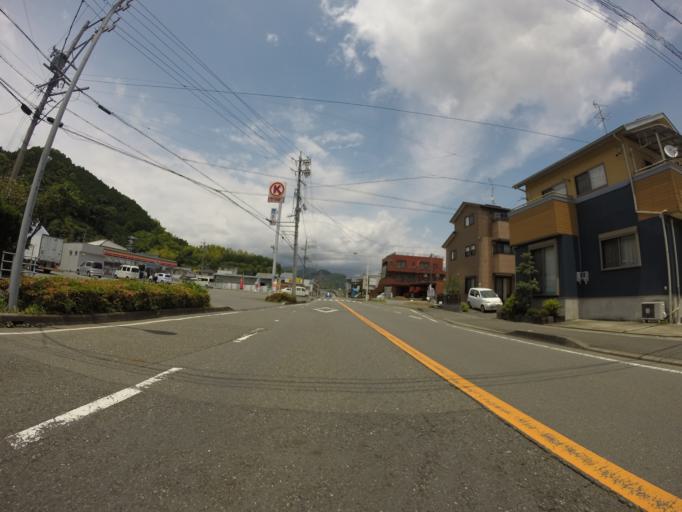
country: JP
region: Shizuoka
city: Shizuoka-shi
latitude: 34.9649
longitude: 138.3564
